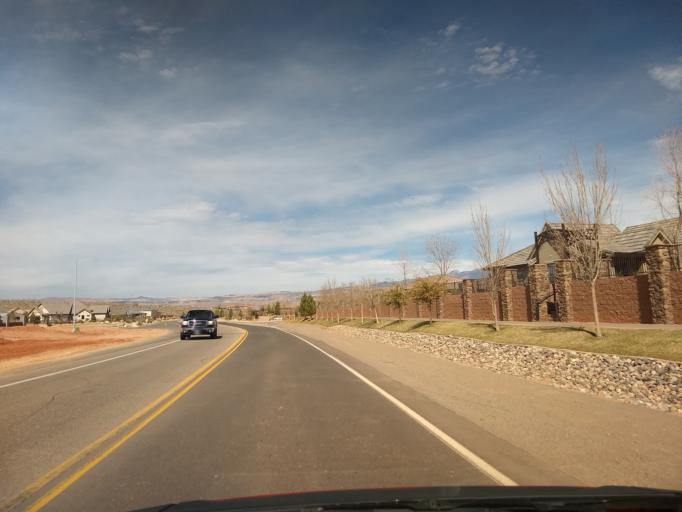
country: US
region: Utah
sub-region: Washington County
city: Washington
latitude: 37.0664
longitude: -113.4912
